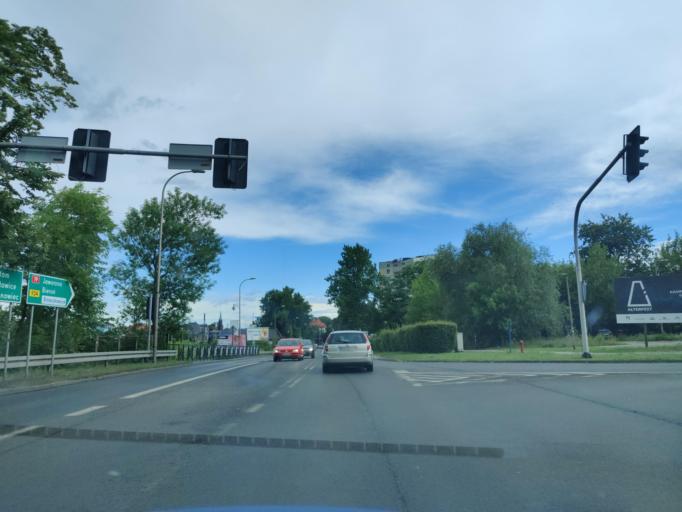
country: PL
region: Silesian Voivodeship
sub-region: Myslowice
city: Myslowice
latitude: 50.2440
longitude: 19.1328
